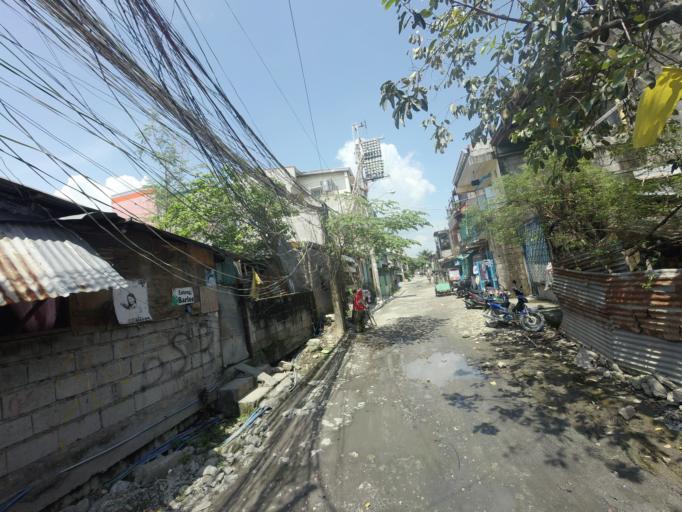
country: PH
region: Calabarzon
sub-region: Province of Rizal
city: Taguig
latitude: 14.5406
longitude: 121.1059
